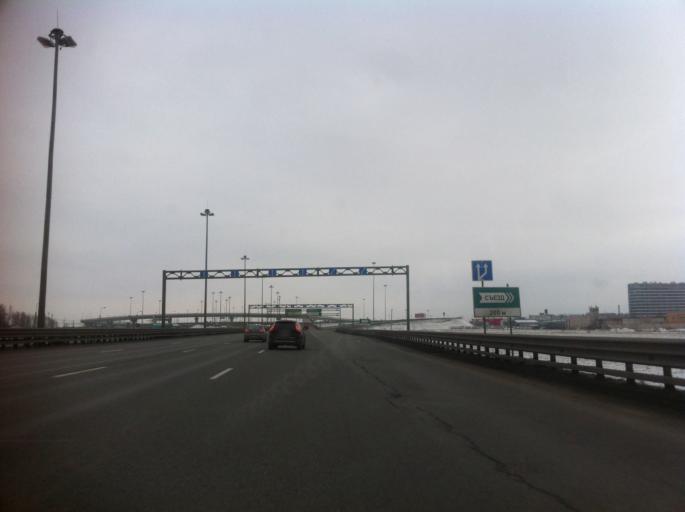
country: RU
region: St.-Petersburg
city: Kupchino
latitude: 59.8155
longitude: 30.3124
